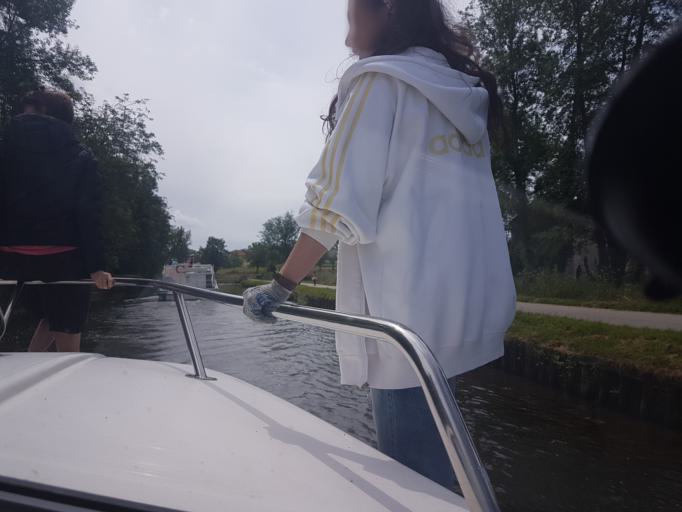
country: FR
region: Bourgogne
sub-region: Departement de l'Yonne
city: Augy
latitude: 47.7846
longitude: 3.5941
